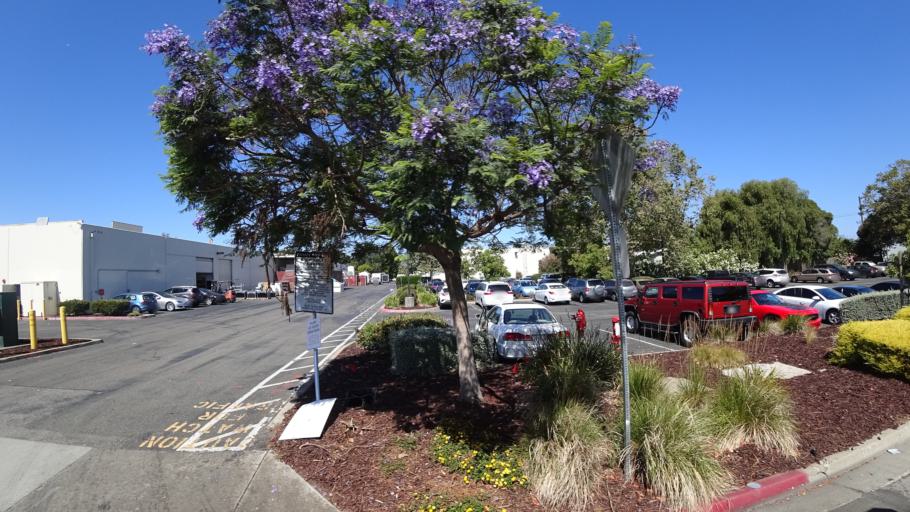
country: US
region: California
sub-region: Alameda County
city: San Lorenzo
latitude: 37.6521
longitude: -122.1309
